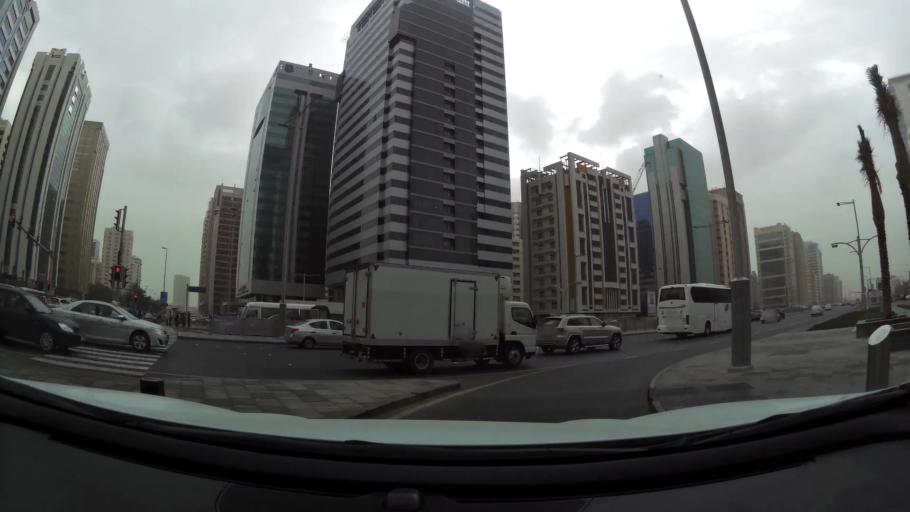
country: AE
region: Abu Dhabi
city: Abu Dhabi
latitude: 24.4945
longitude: 54.3749
